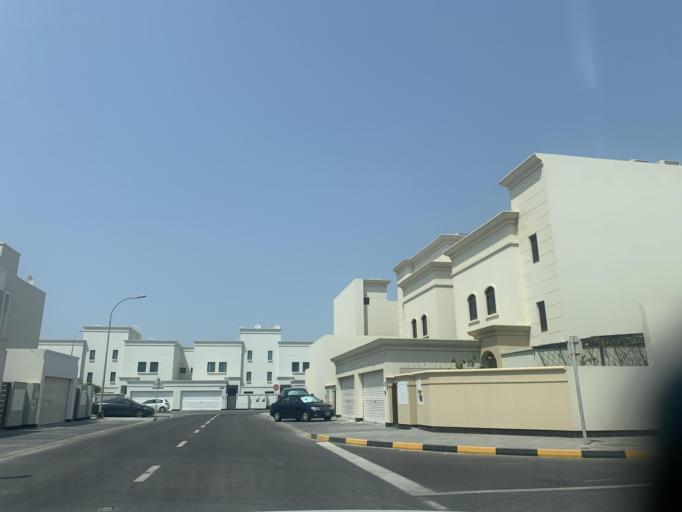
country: BH
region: Muharraq
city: Al Muharraq
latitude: 26.3036
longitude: 50.6287
